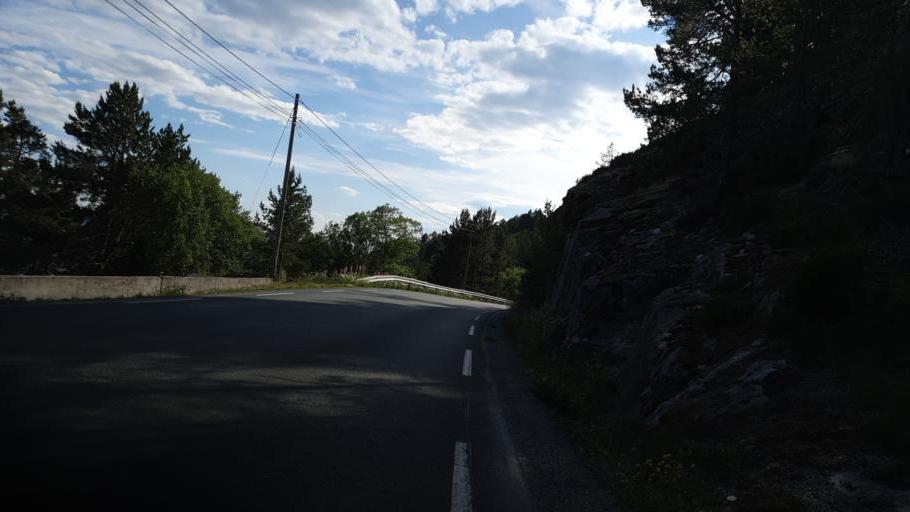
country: NO
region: Sor-Trondelag
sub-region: Trondheim
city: Trondheim
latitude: 63.5709
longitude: 10.3462
